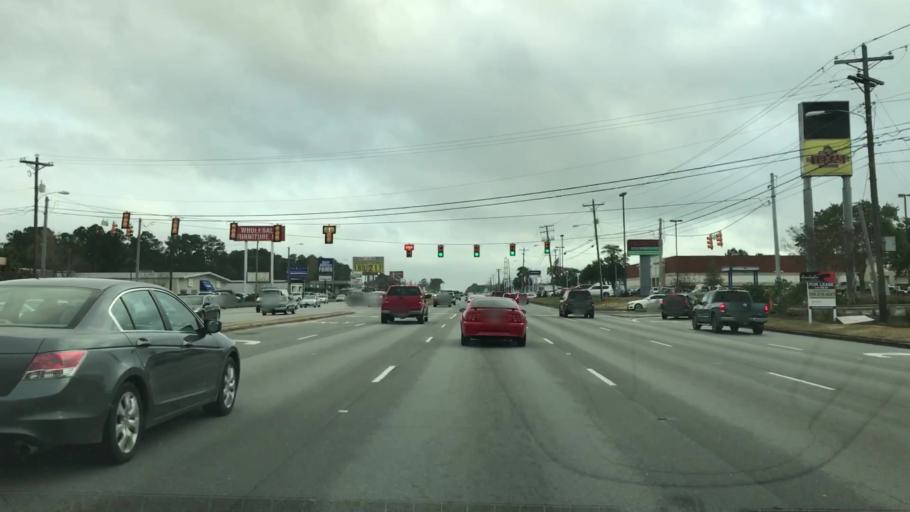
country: US
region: South Carolina
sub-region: Berkeley County
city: Goose Creek
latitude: 32.9636
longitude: -80.0441
